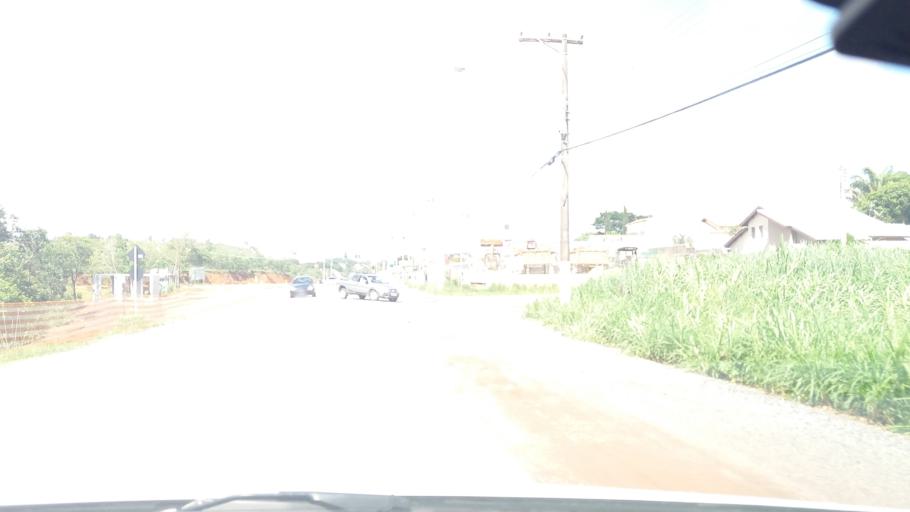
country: BR
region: Sao Paulo
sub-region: Atibaia
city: Atibaia
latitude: -23.1083
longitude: -46.5233
